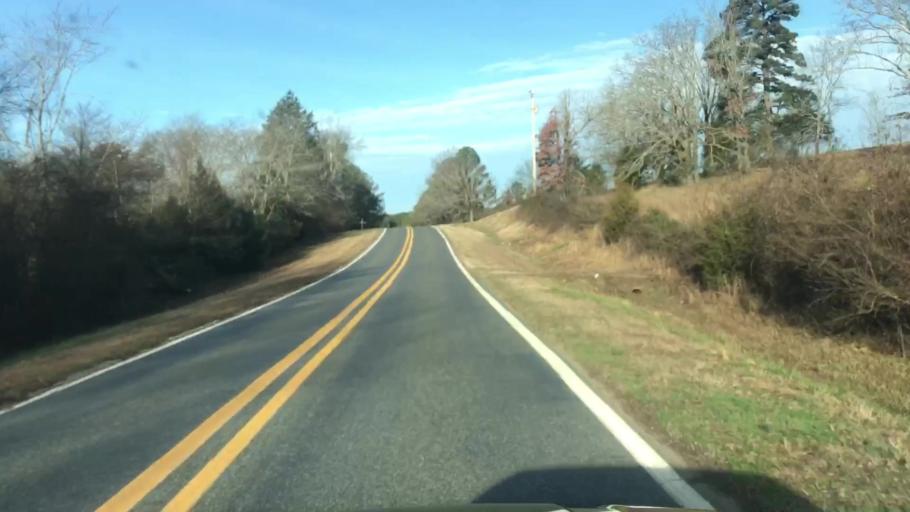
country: US
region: Arkansas
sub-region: Garland County
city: Rockwell
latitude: 34.4770
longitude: -93.2651
